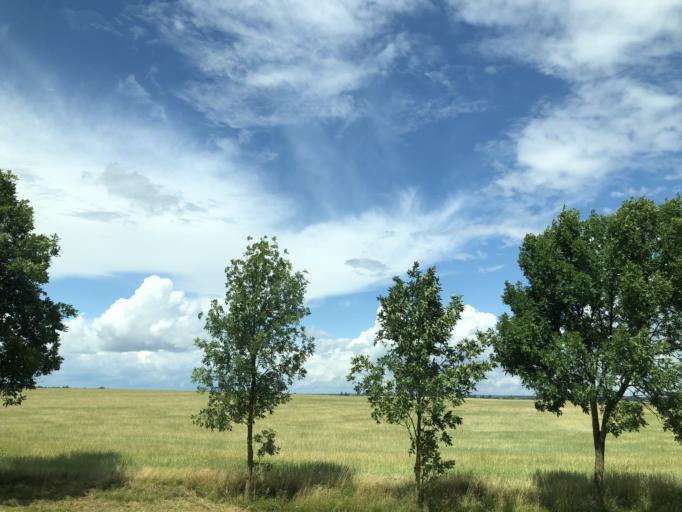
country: BY
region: Minsk
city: Tsimkavichy
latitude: 53.2507
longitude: 26.9044
